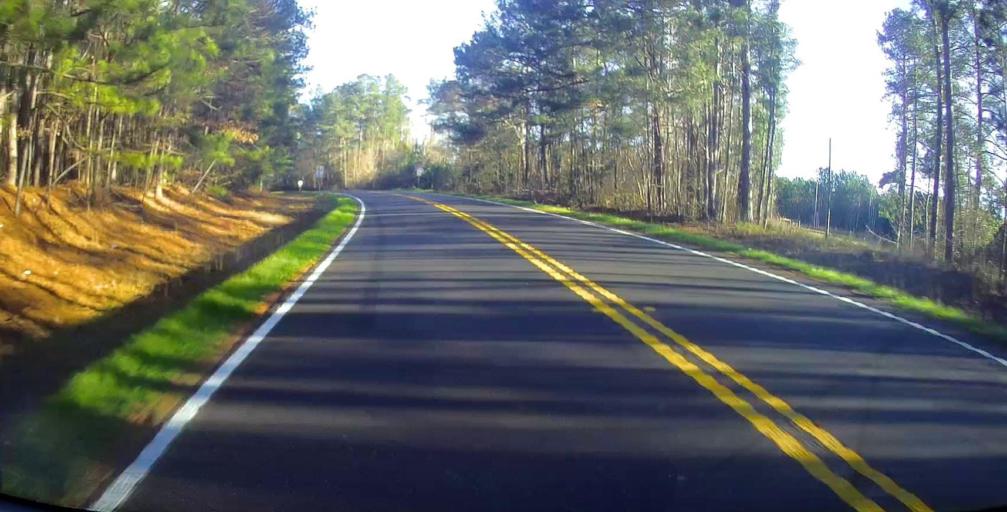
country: US
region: Georgia
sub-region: Meriwether County
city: Manchester
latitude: 32.8950
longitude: -84.7141
